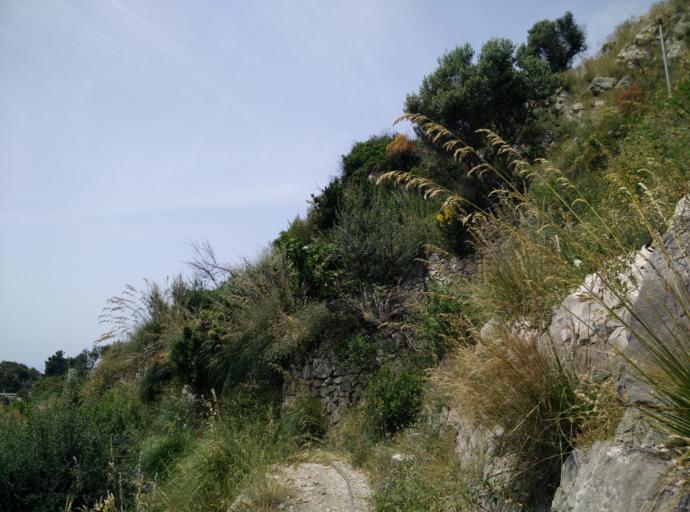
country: IT
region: Campania
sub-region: Provincia di Napoli
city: Massa Lubrense
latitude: 40.5800
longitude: 14.3454
